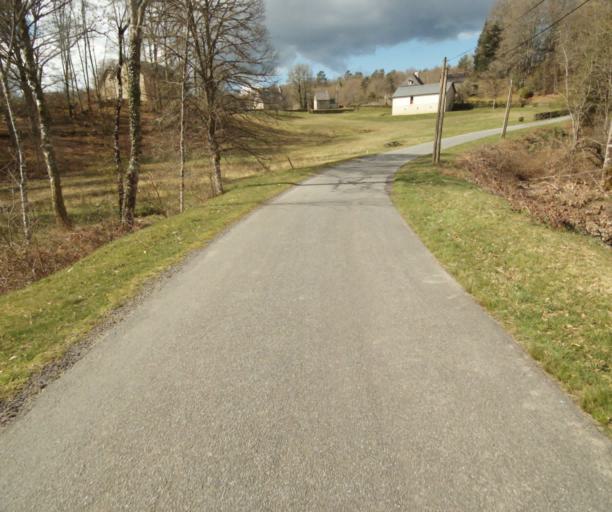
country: FR
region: Limousin
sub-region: Departement de la Correze
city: Argentat
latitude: 45.2396
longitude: 1.9553
